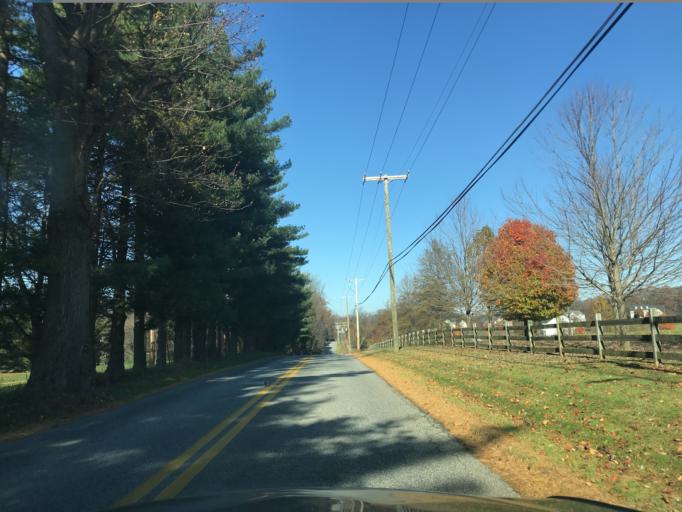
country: US
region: Maryland
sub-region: Baltimore County
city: Hampton
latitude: 39.4996
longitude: -76.5488
